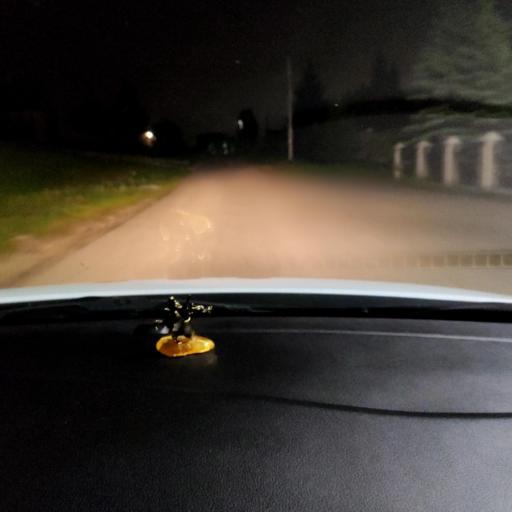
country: RU
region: Tatarstan
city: Stolbishchi
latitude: 55.6311
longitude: 49.1450
